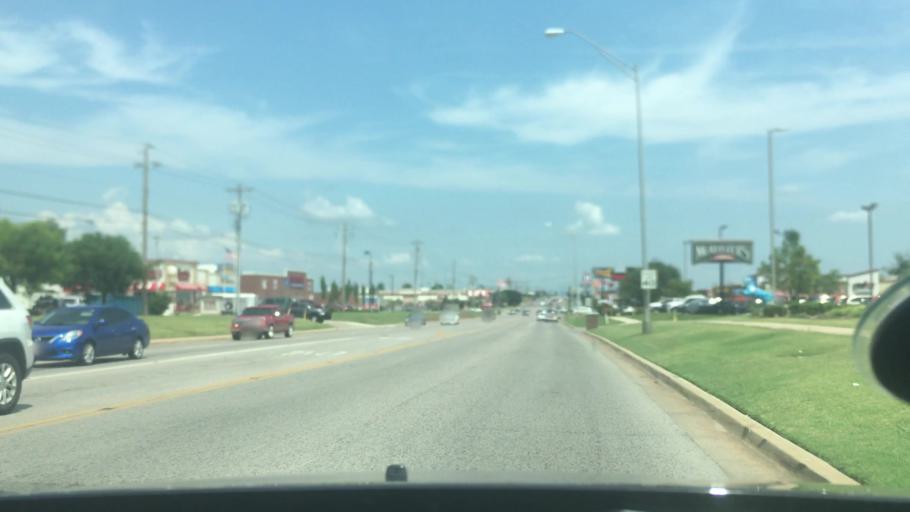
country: US
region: Oklahoma
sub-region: Pottawatomie County
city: Shawnee
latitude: 35.3764
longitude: -96.9297
